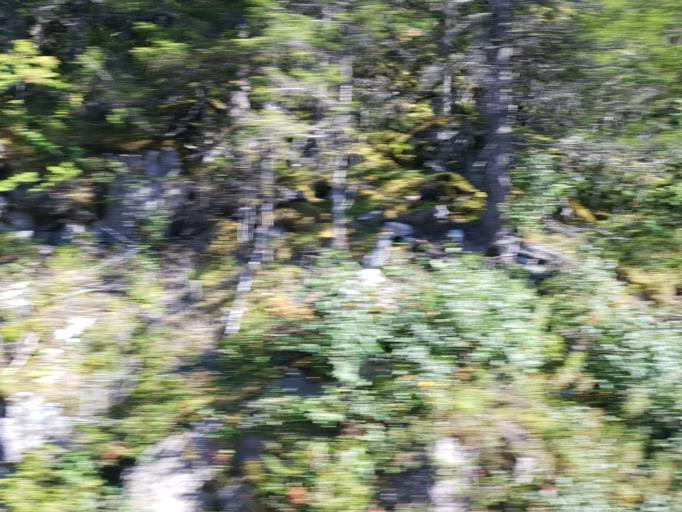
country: NO
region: Sor-Trondelag
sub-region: Afjord
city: A i Afjord
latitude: 63.7412
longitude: 10.2362
